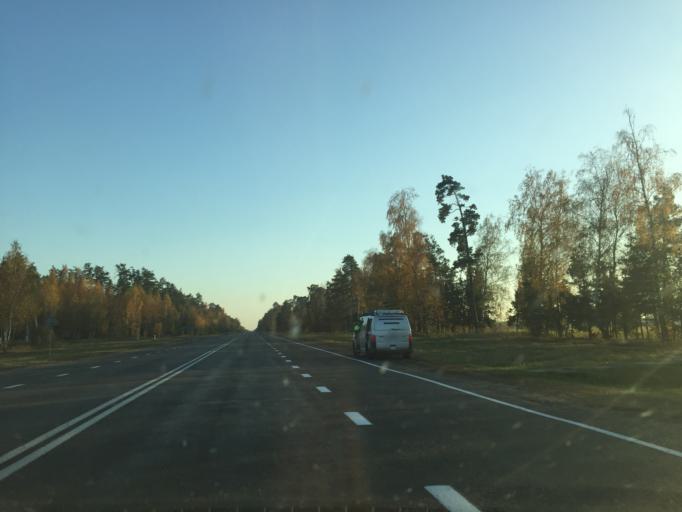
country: BY
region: Mogilev
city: Poselok Voskhod
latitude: 53.7316
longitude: 30.3667
